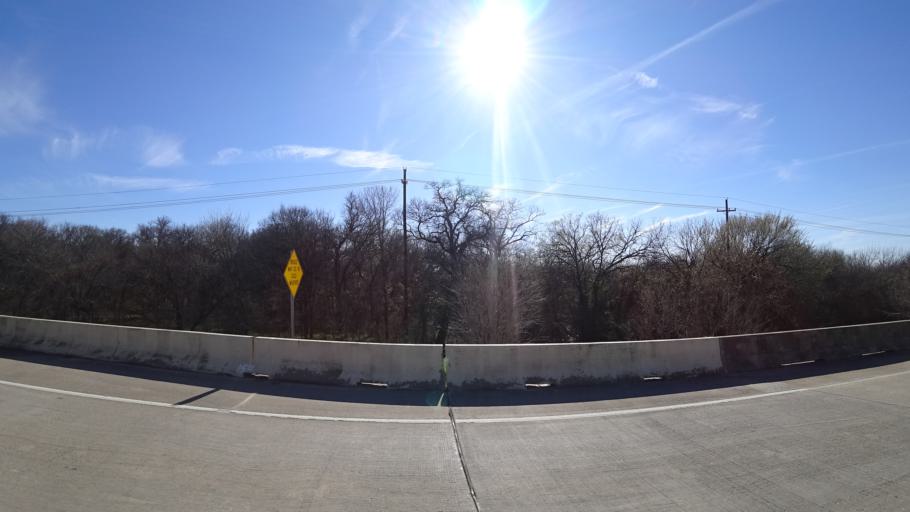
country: US
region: Texas
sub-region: Denton County
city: Lewisville
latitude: 32.9966
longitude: -96.9551
